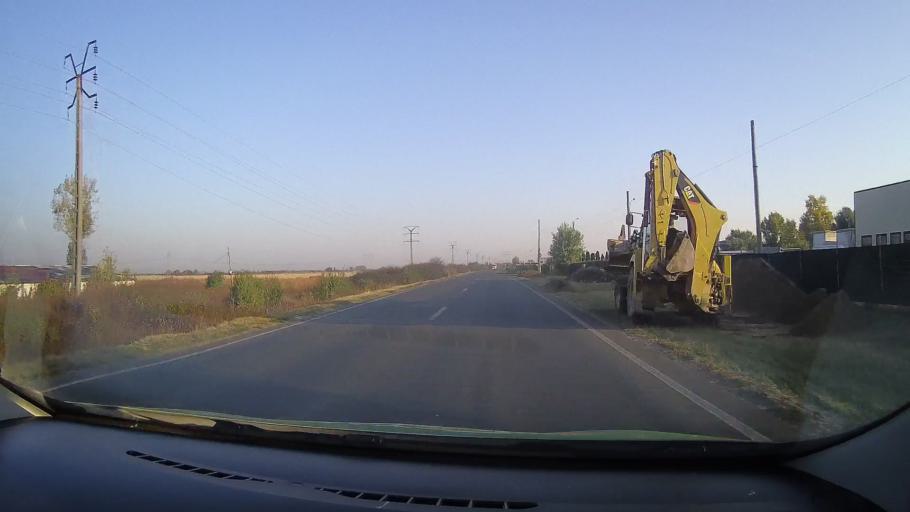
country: RO
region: Arad
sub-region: Comuna Sofronea
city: Sofronea
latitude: 46.2283
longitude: 21.3204
